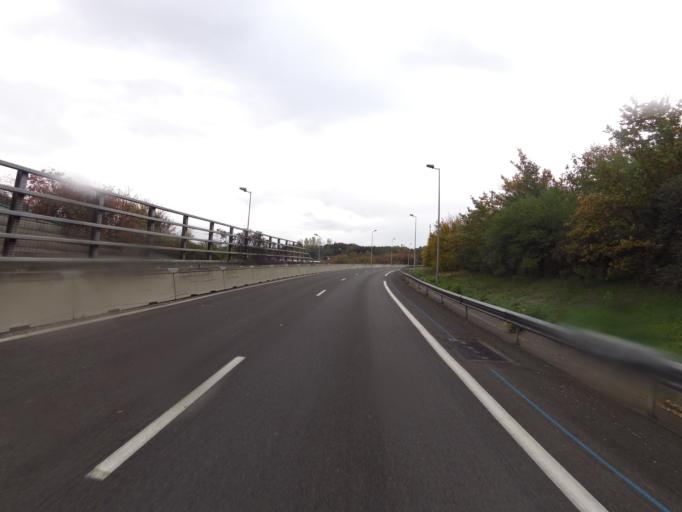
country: FR
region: Rhone-Alpes
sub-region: Departement de l'Isere
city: Chasse-sur-Rhone
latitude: 45.5881
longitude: 4.7995
